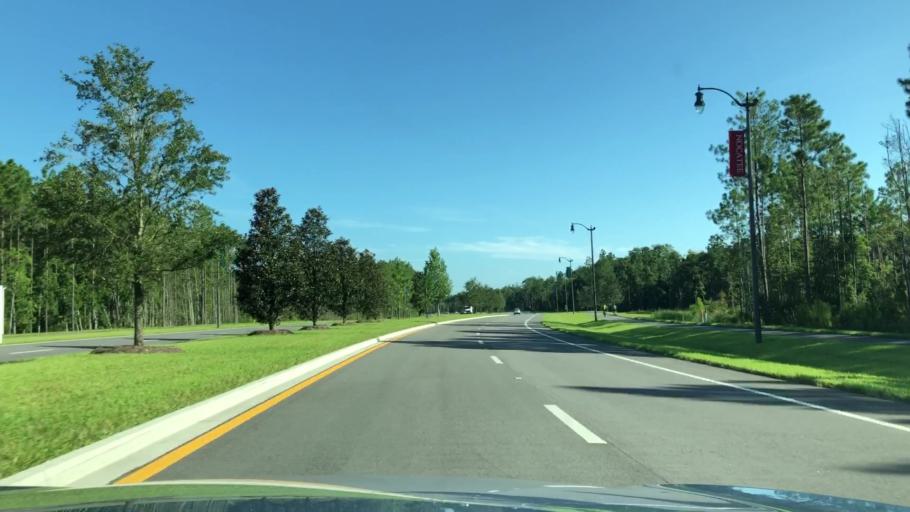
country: US
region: Florida
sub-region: Saint Johns County
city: Palm Valley
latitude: 30.0853
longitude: -81.4053
